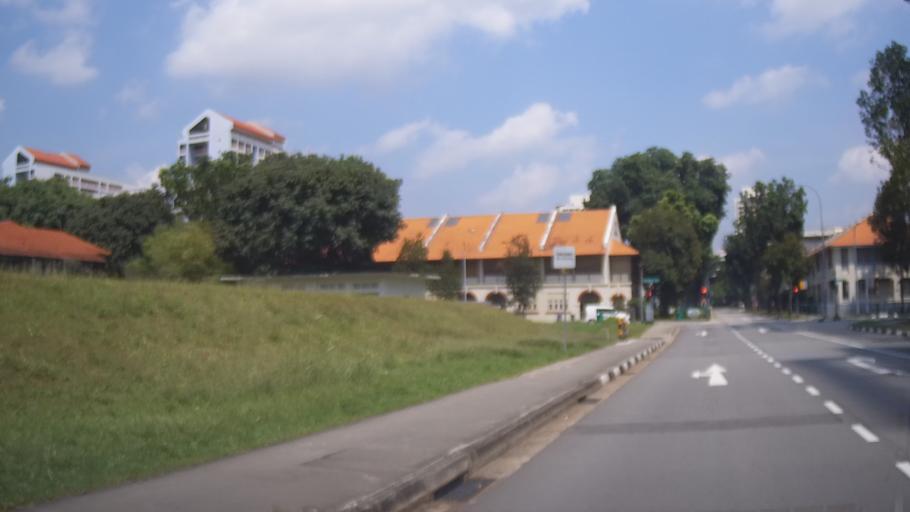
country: SG
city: Singapore
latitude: 1.3195
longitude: 103.8591
